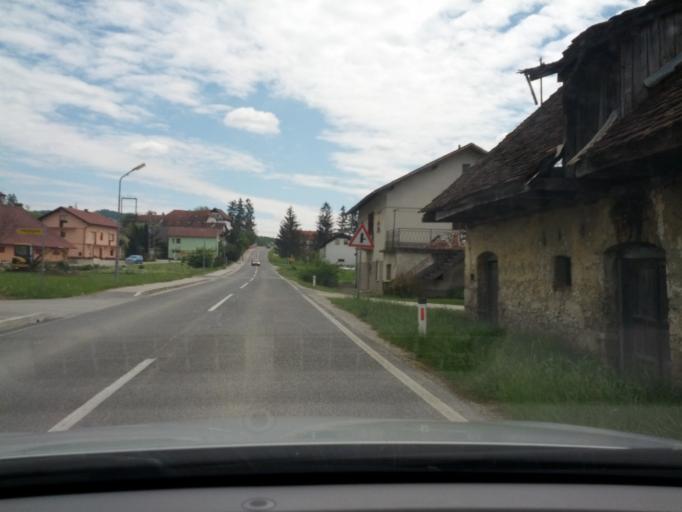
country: SI
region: Podcetrtek
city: Podcetrtek
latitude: 46.1973
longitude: 15.5950
